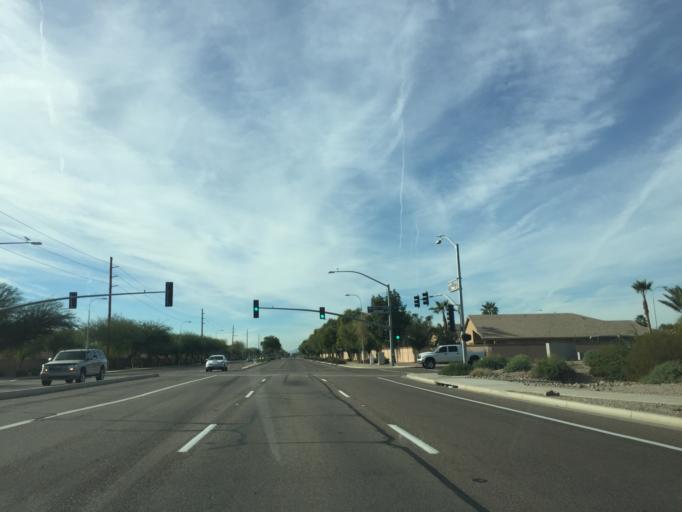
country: US
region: Arizona
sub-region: Maricopa County
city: Chandler
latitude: 33.2919
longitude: -111.7977
